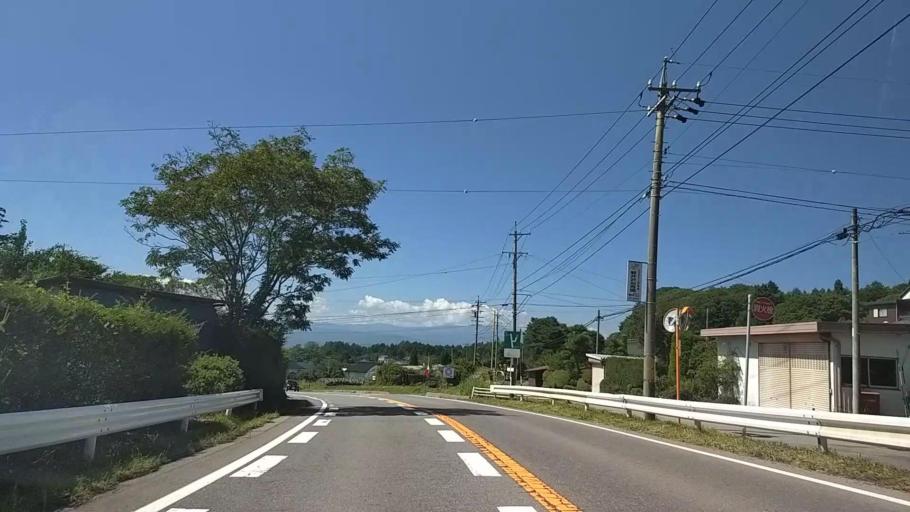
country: JP
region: Nagano
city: Komoro
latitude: 36.3415
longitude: 138.5218
